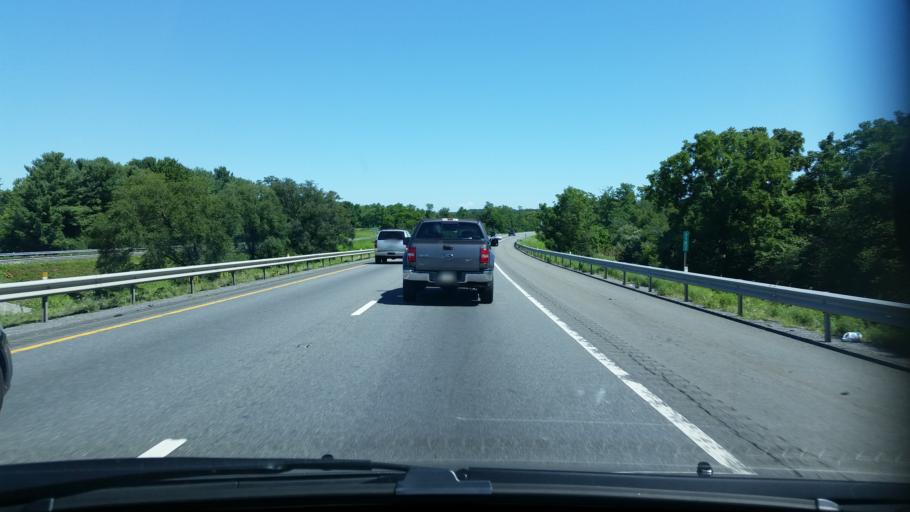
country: US
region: Virginia
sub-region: City of Winchester
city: Winchester
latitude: 39.2248
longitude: -78.1375
